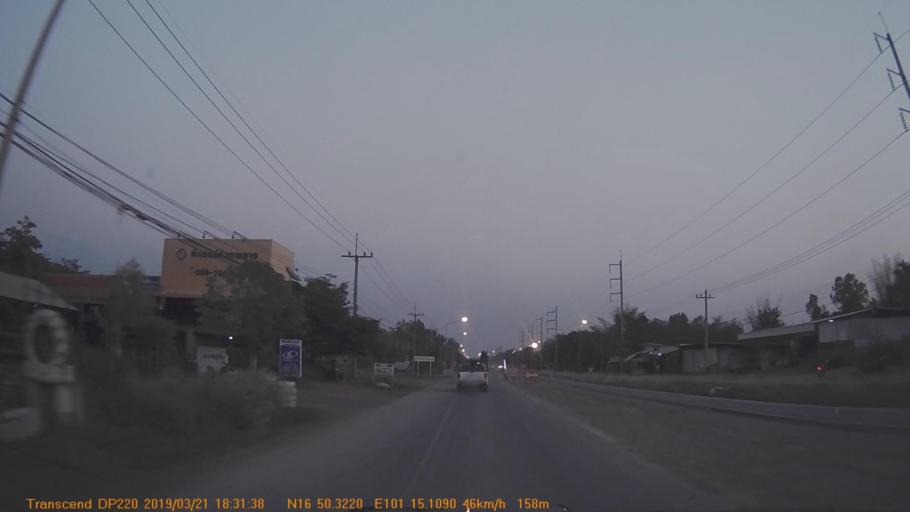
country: TH
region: Phetchabun
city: Lom Kao
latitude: 16.8385
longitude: 101.2519
